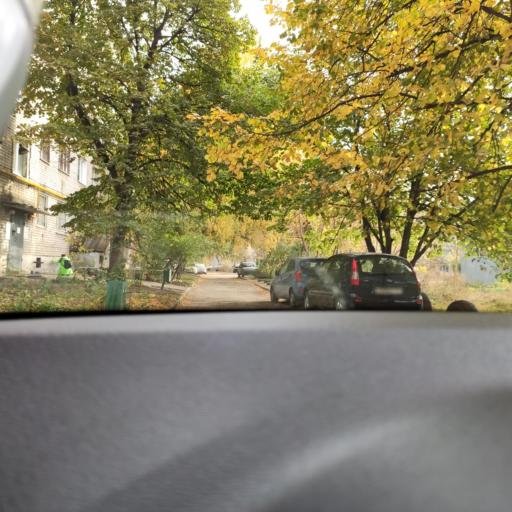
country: RU
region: Samara
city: Samara
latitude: 53.2115
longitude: 50.2418
